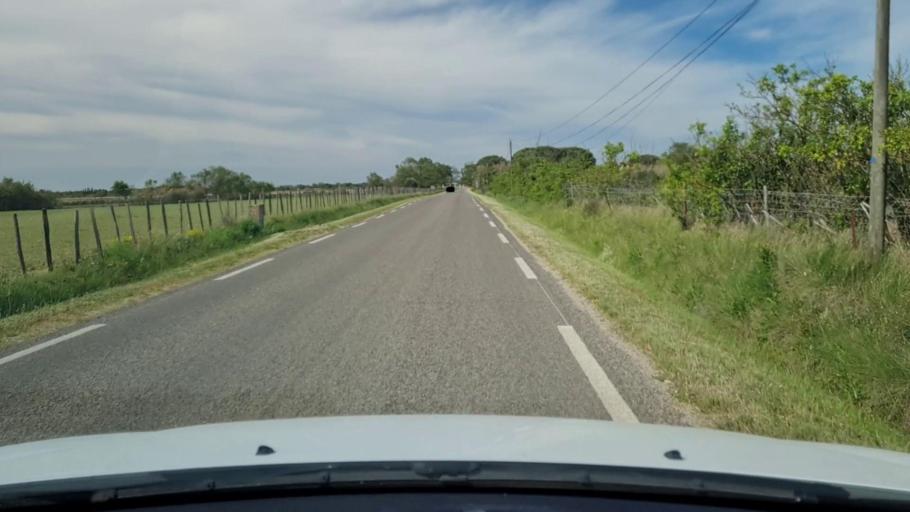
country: FR
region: Languedoc-Roussillon
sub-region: Departement du Gard
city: Aigues-Mortes
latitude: 43.6004
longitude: 4.2102
